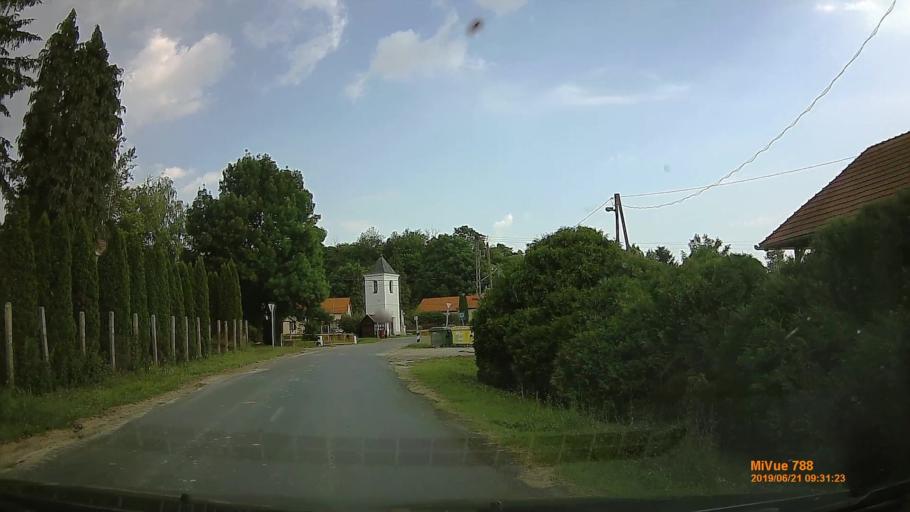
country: HU
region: Somogy
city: Taszar
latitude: 46.3051
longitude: 17.8813
